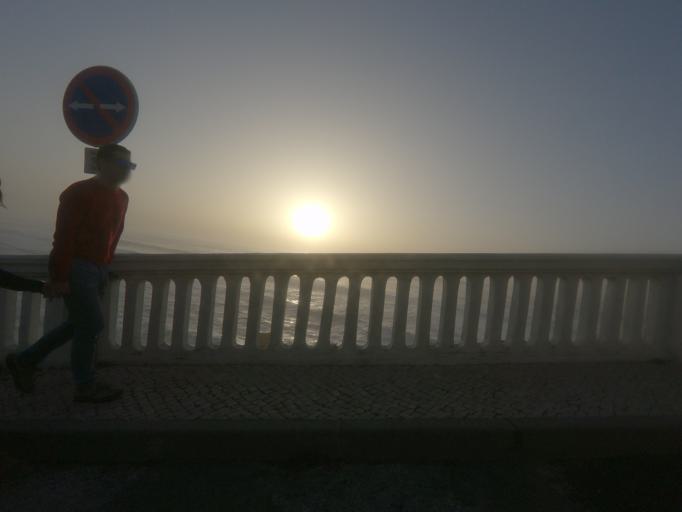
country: PT
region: Leiria
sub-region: Alcobaca
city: Pataias
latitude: 39.7571
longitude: -9.0324
